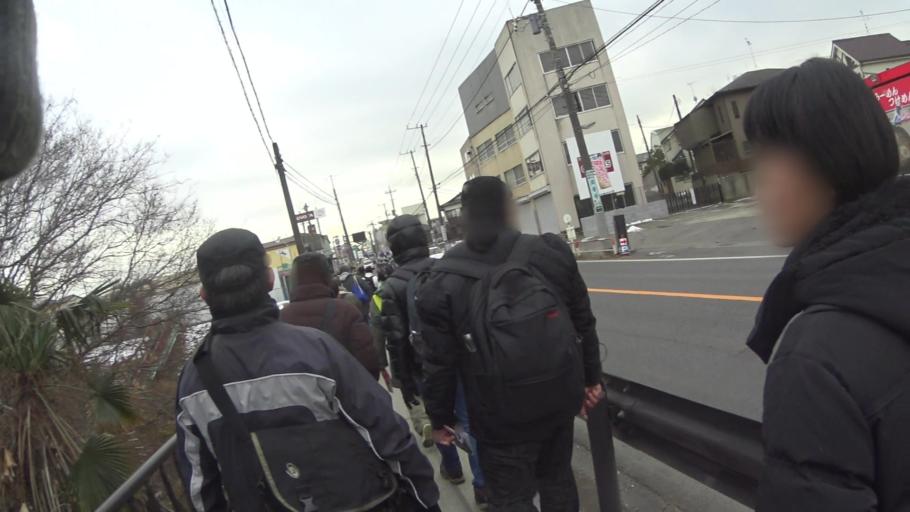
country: JP
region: Chiba
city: Funabashi
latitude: 35.7511
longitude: 139.9994
